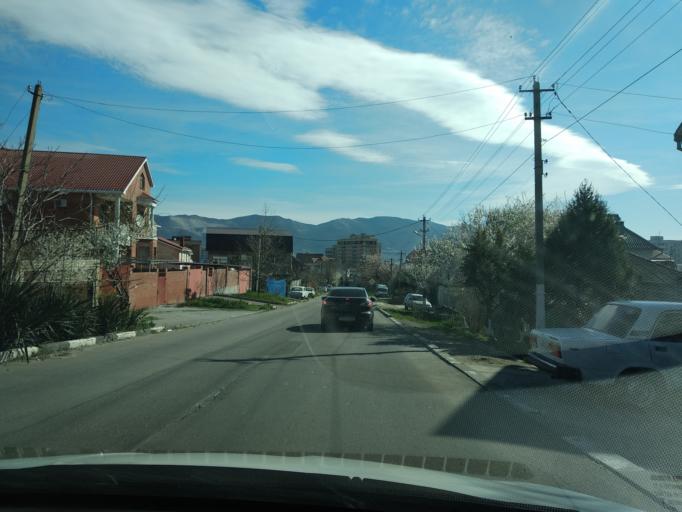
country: RU
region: Krasnodarskiy
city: Novorossiysk
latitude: 44.7033
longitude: 37.7777
